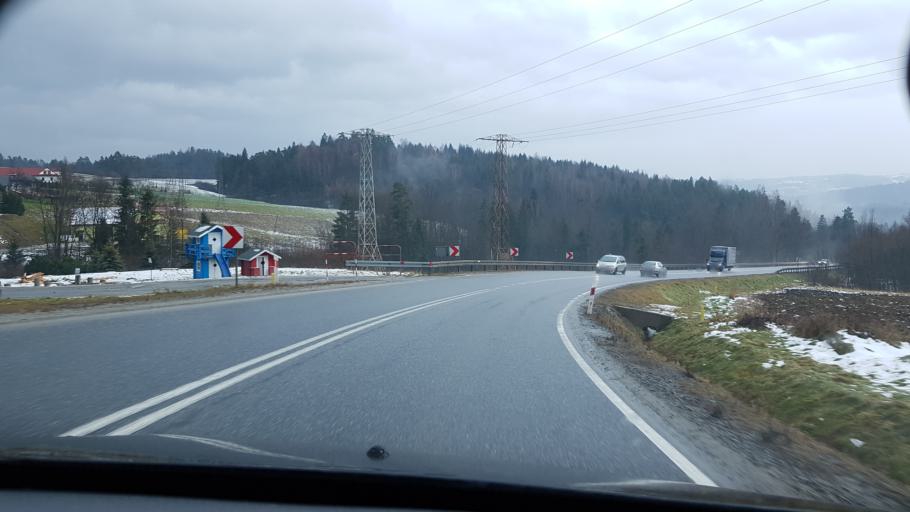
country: PL
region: Lesser Poland Voivodeship
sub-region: Powiat suski
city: Osielec
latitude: 49.6679
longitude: 19.7980
